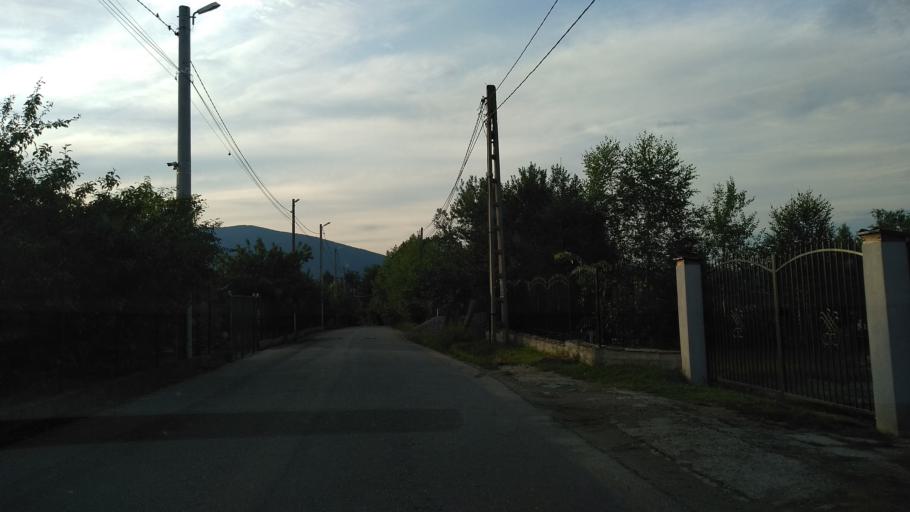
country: RO
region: Hunedoara
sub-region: Municipiul  Vulcan
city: Jiu-Paroseni
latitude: 45.3591
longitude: 23.2875
